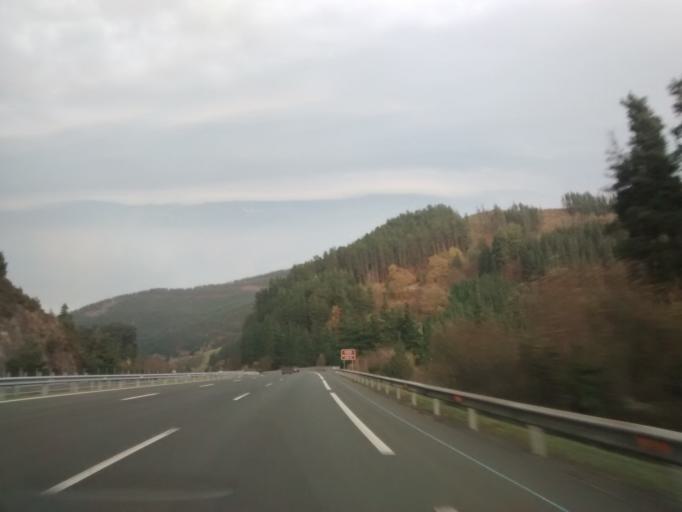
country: ES
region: Basque Country
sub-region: Provincia de Alava
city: Lezama
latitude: 43.0723
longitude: -2.9228
